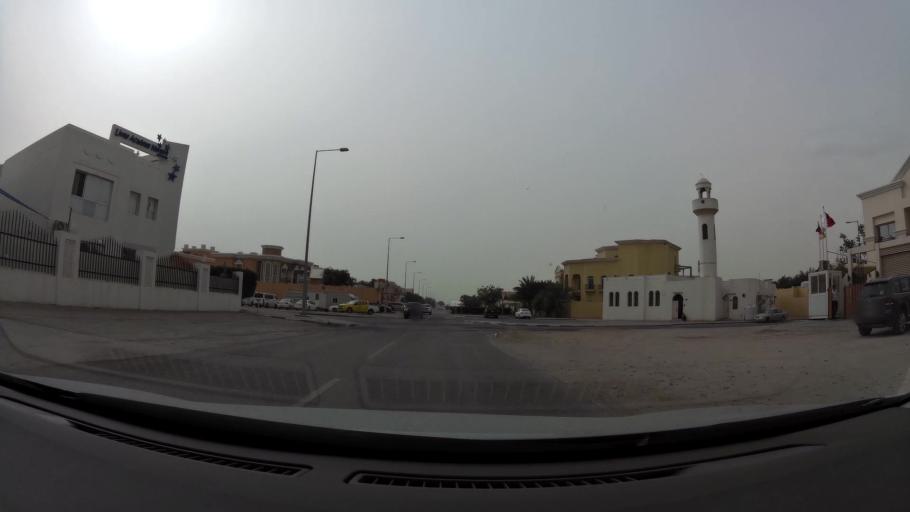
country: QA
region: Baladiyat ad Dawhah
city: Doha
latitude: 25.2503
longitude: 51.4991
